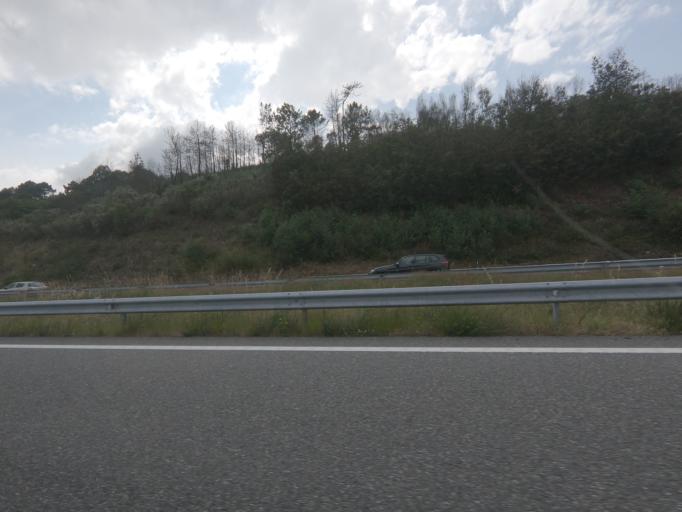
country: ES
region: Galicia
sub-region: Provincia de Ourense
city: Melon
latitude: 42.2463
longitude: -8.2261
